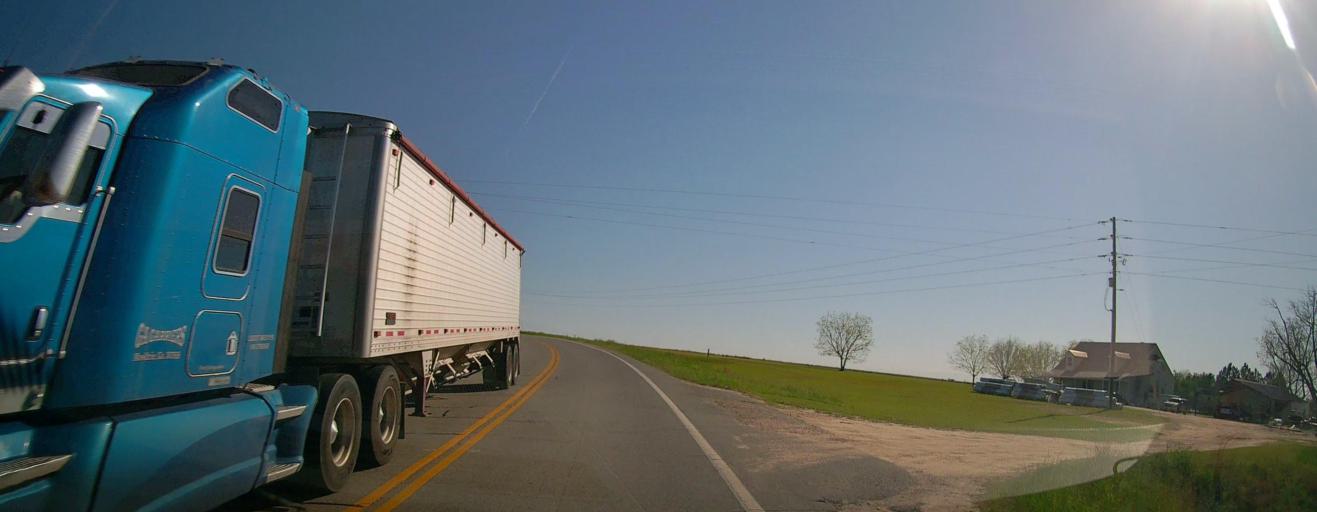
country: US
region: Georgia
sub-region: Wilcox County
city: Rochelle
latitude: 31.9260
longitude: -83.4656
